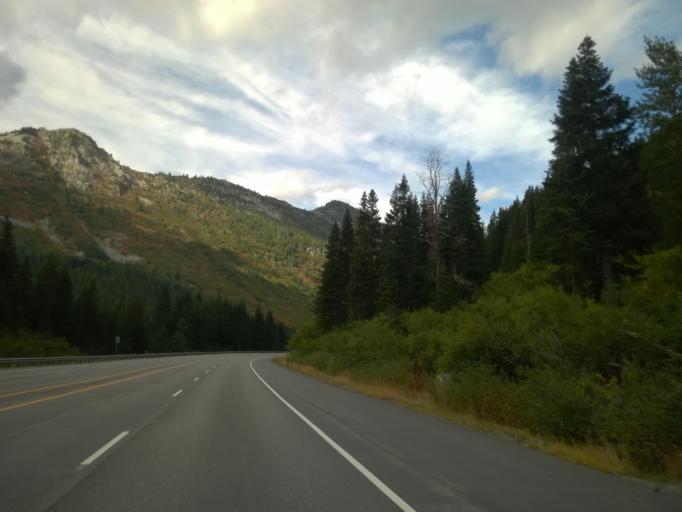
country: US
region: Washington
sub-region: Chelan County
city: Leavenworth
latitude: 47.7664
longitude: -121.0776
